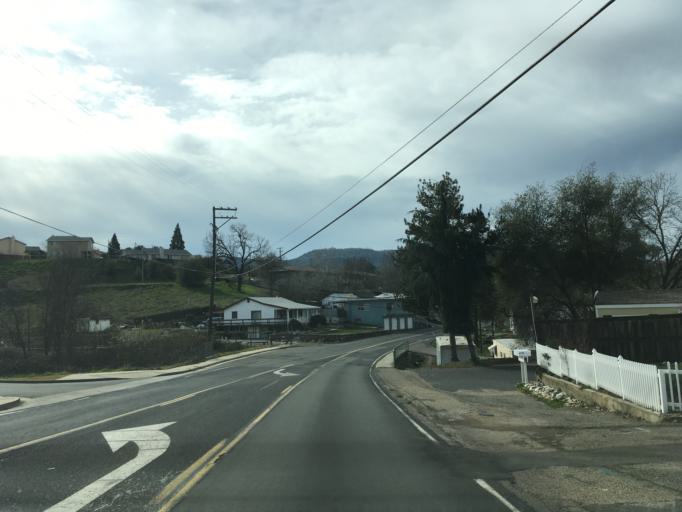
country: US
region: California
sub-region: Calaveras County
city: San Andreas
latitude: 38.1897
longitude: -120.6719
